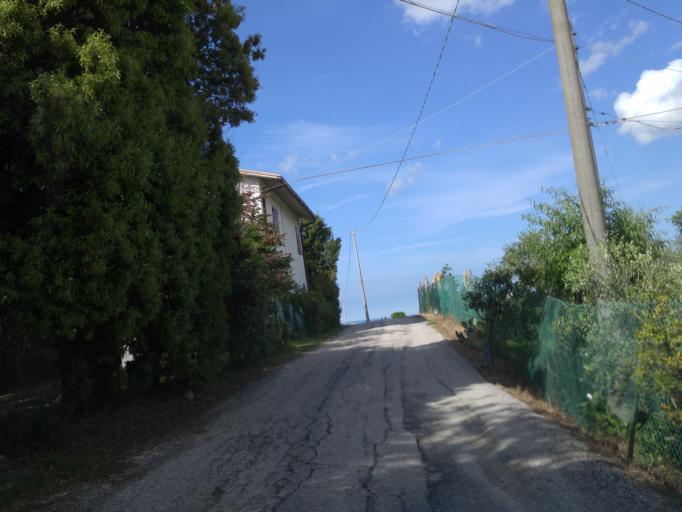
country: IT
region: The Marches
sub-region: Provincia di Pesaro e Urbino
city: Piagge
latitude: 43.7530
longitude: 12.9722
